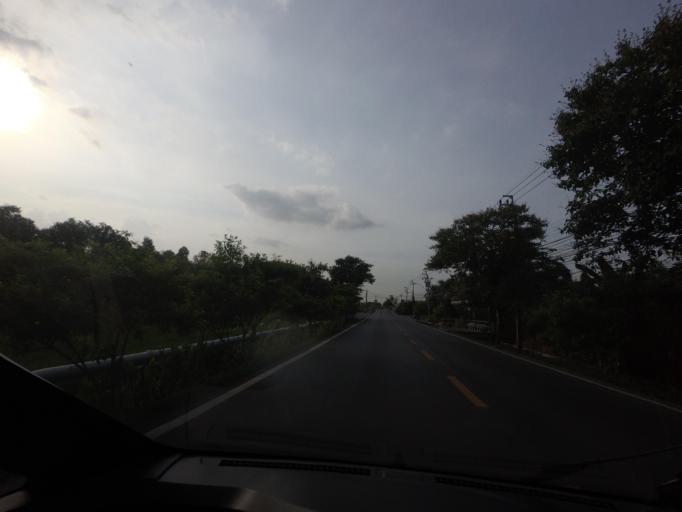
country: TH
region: Bangkok
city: Nong Chok
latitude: 13.8383
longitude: 100.8696
